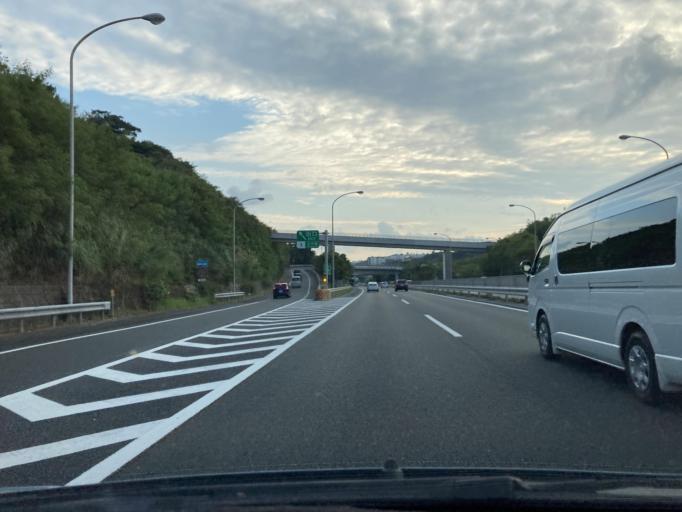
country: JP
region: Okinawa
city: Chatan
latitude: 26.2925
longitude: 127.7897
